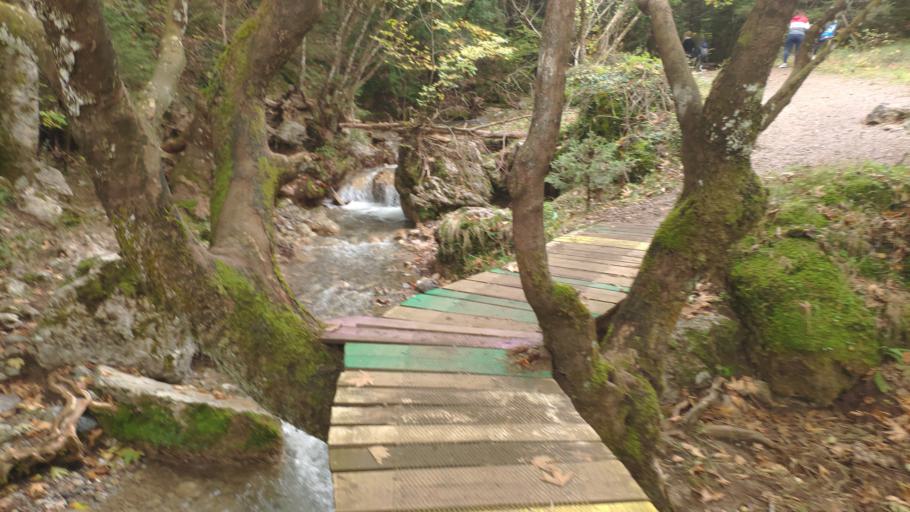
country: GR
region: Central Greece
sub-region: Nomos Fthiotidos
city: Stavros
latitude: 38.7370
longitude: 22.3383
